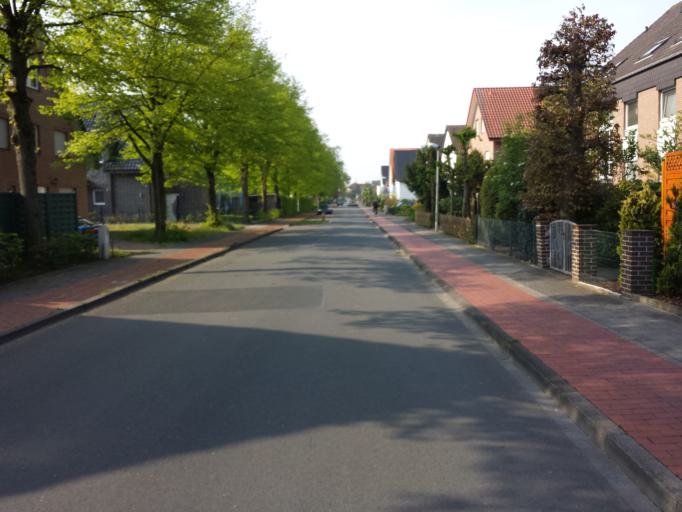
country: DE
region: North Rhine-Westphalia
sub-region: Regierungsbezirk Detmold
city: Guetersloh
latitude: 51.8921
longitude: 8.3721
